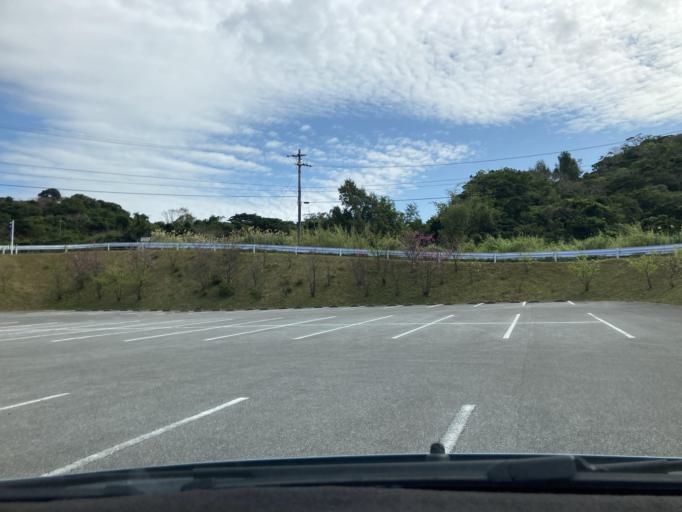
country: JP
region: Okinawa
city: Nago
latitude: 26.6902
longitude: 127.9272
